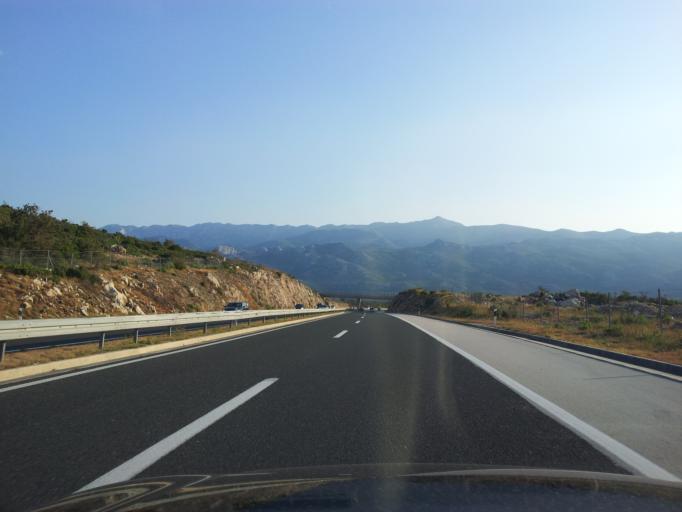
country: HR
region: Zadarska
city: Posedarje
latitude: 44.2279
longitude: 15.5099
